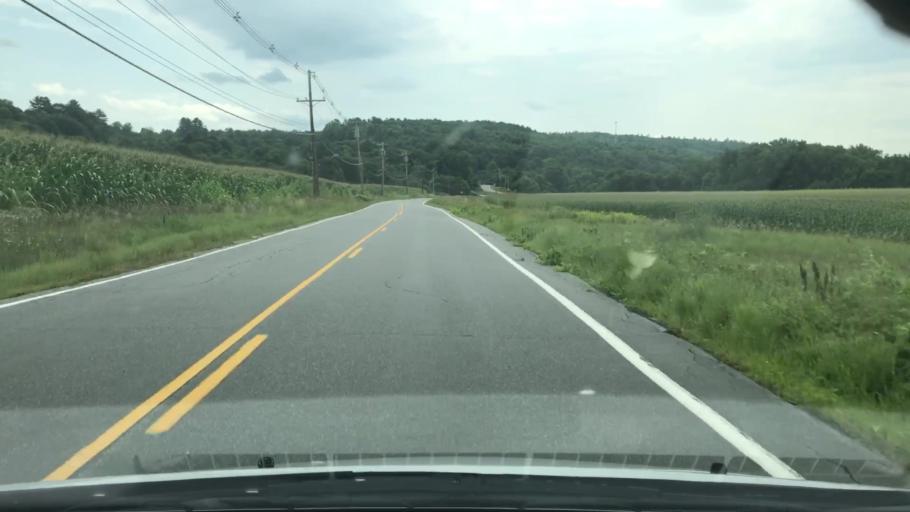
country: US
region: New Hampshire
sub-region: Grafton County
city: Woodsville
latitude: 44.1384
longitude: -72.0332
